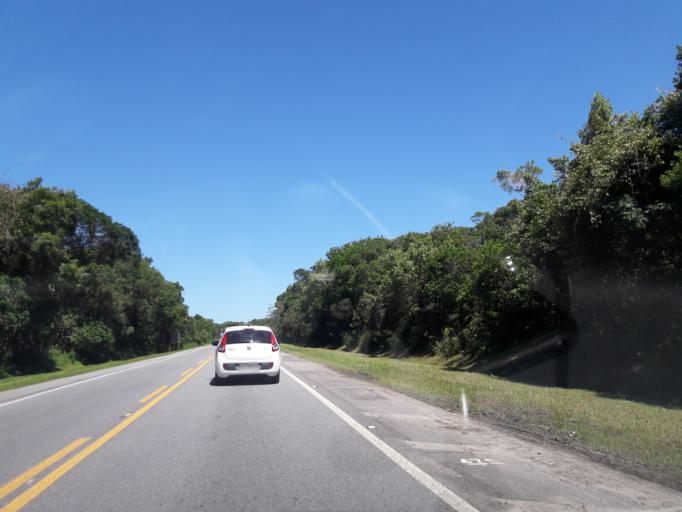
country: BR
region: Parana
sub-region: Pontal Do Parana
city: Pontal do Parana
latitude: -25.6674
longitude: -48.5170
